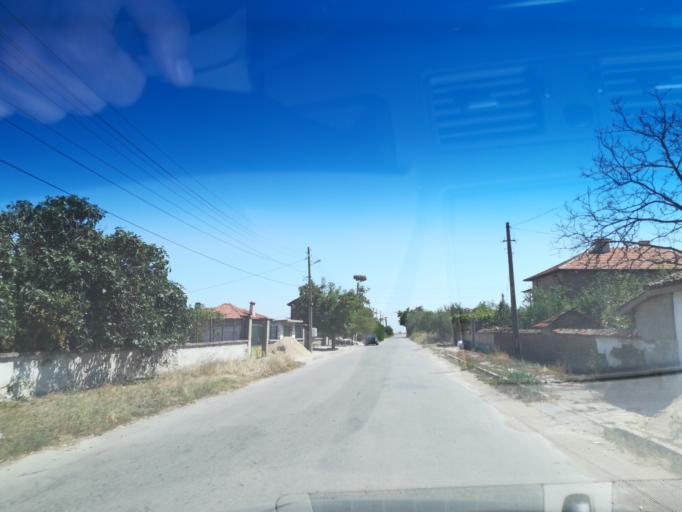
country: BG
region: Pazardzhik
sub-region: Obshtina Pazardzhik
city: Pazardzhik
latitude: 42.3288
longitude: 24.4042
